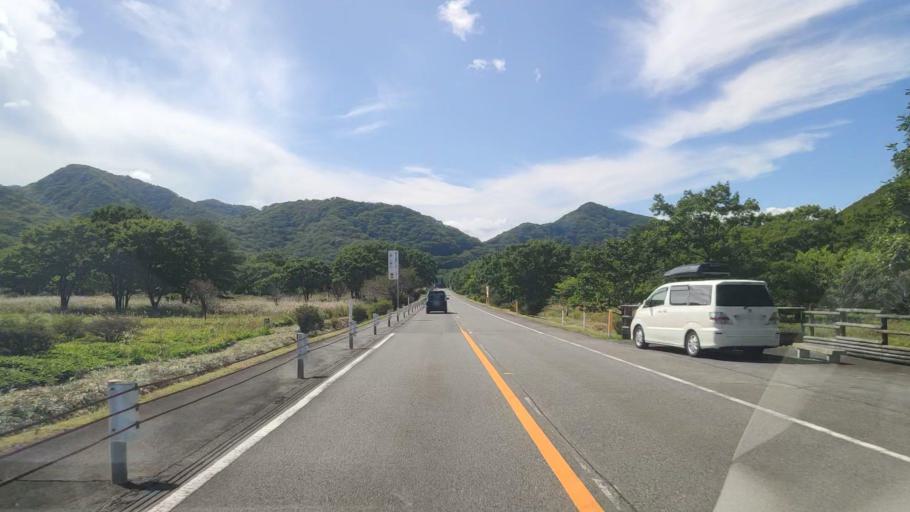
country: JP
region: Gunma
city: Shibukawa
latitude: 36.4743
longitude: 138.8872
